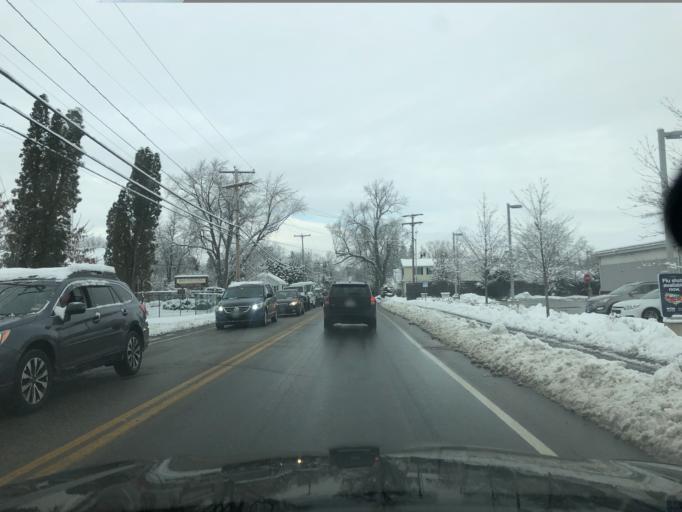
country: US
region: New Hampshire
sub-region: Strafford County
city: Somersworth
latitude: 43.2478
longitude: -70.8738
